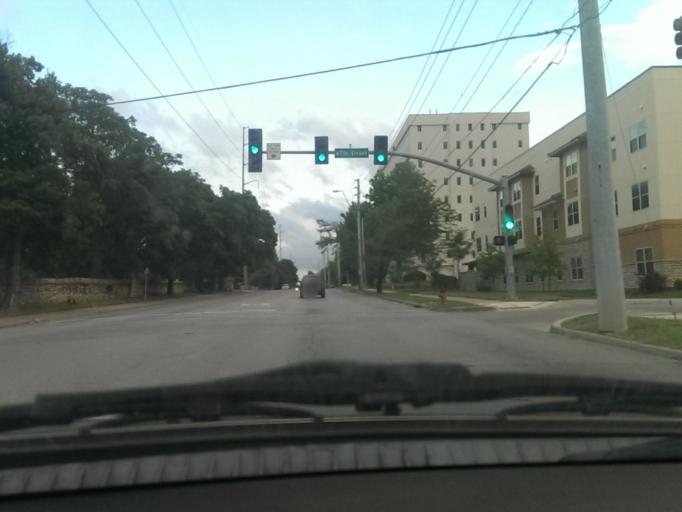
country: US
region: Kansas
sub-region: Johnson County
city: Mission Hills
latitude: 39.0063
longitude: -94.5750
